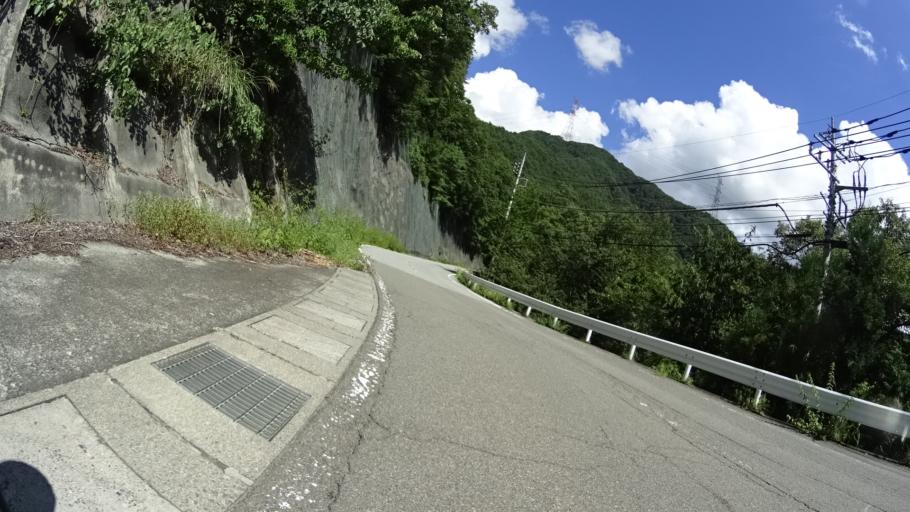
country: JP
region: Yamanashi
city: Enzan
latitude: 35.6579
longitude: 138.8125
